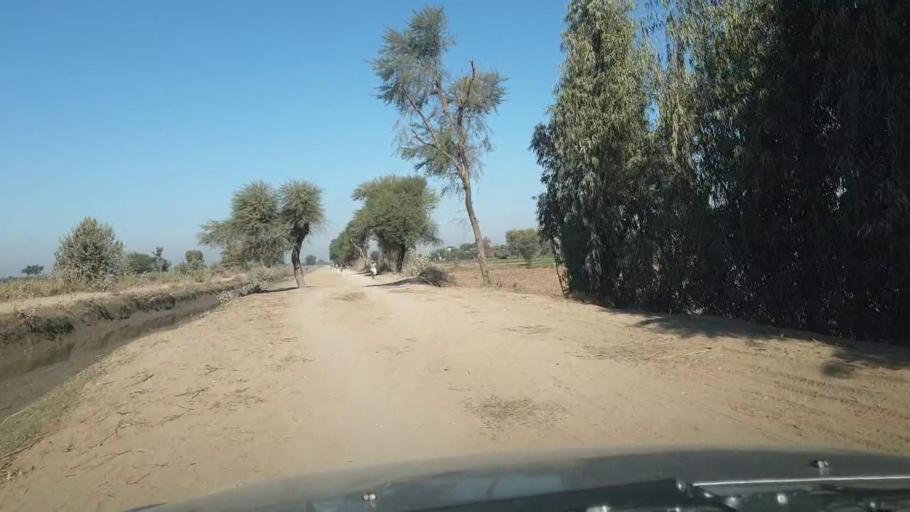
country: PK
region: Sindh
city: Ghotki
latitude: 28.0739
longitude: 69.3478
